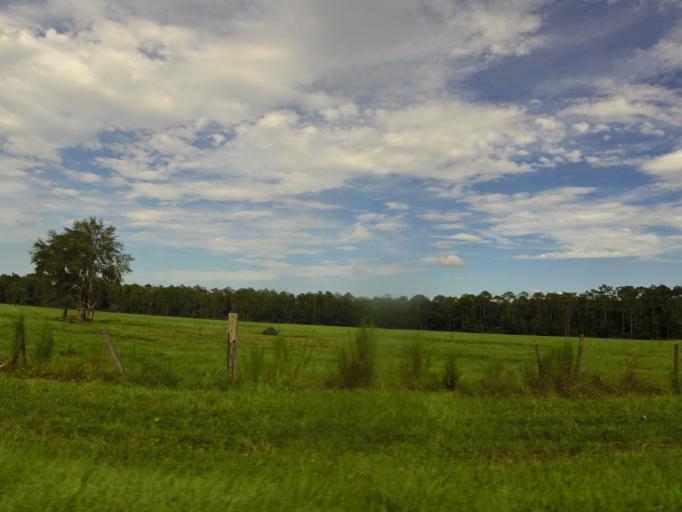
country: US
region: Florida
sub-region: Clay County
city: Green Cove Springs
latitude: 29.9445
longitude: -81.6642
